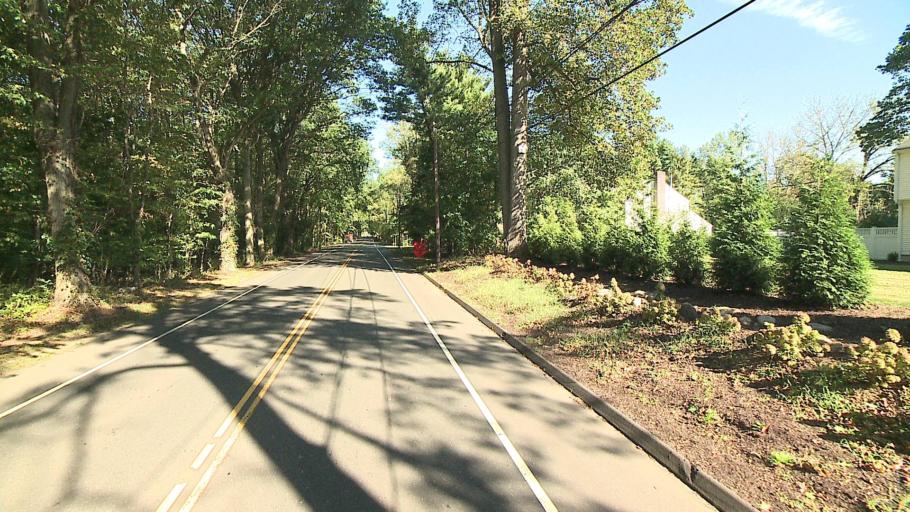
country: US
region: Connecticut
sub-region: Fairfield County
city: New Canaan
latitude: 41.1222
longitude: -73.4836
